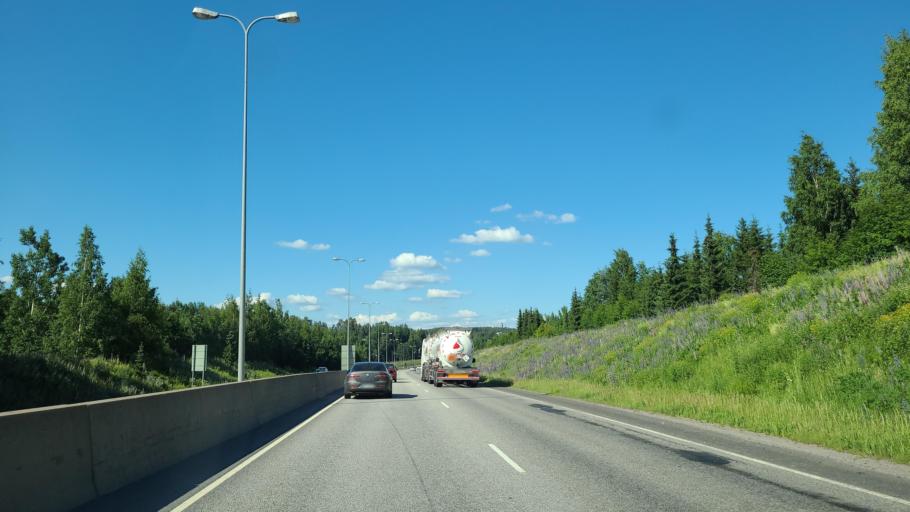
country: FI
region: Central Finland
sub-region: Jyvaeskylae
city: Jyvaeskylae
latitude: 62.2225
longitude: 25.7256
